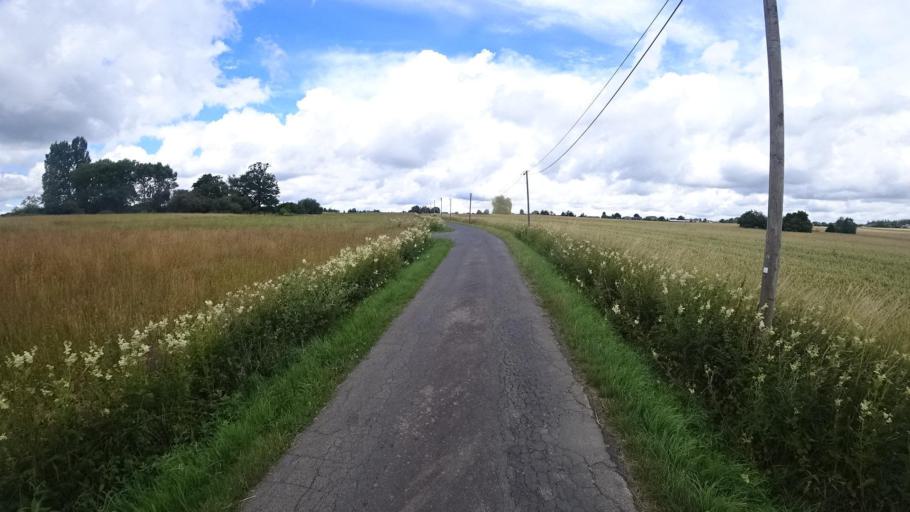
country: DE
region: Rheinland-Pfalz
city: Kircheib
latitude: 50.7020
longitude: 7.4564
